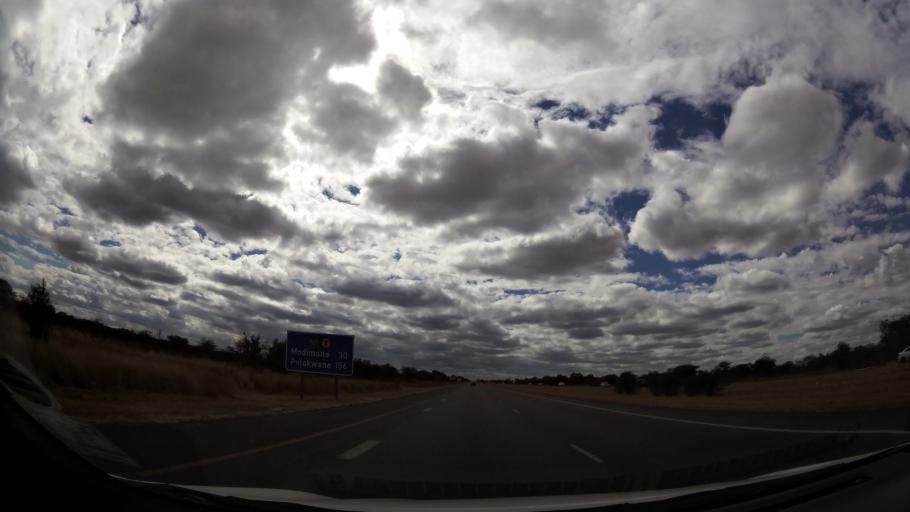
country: ZA
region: Limpopo
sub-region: Waterberg District Municipality
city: Bela-Bela
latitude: -24.9121
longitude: 28.3749
